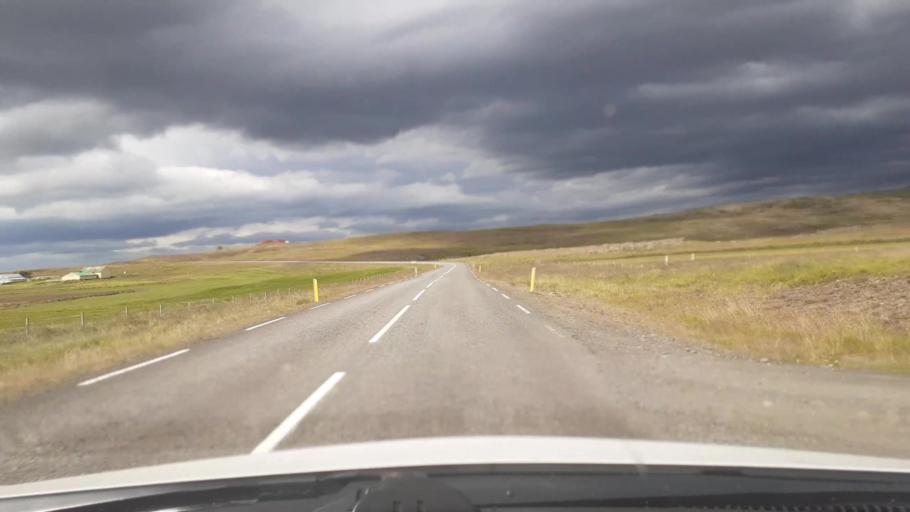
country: IS
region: West
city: Borgarnes
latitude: 64.5457
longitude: -21.6444
